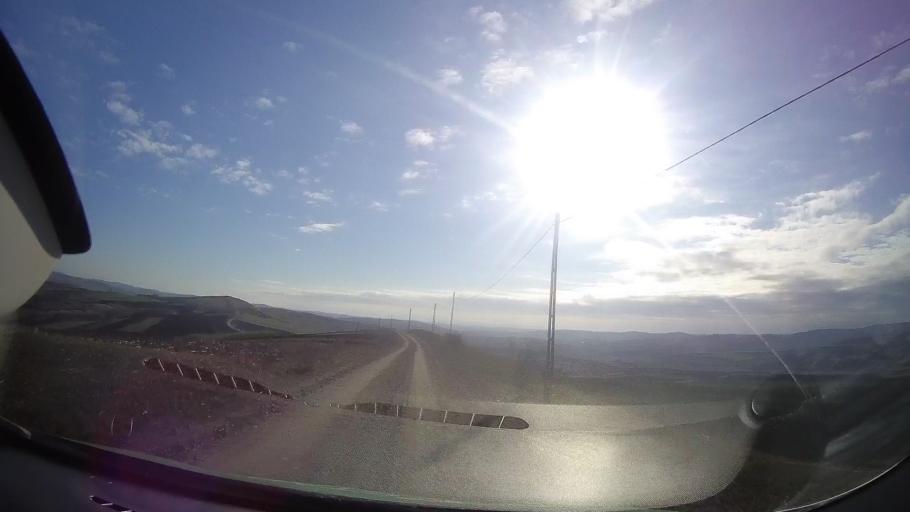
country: RO
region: Mures
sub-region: Comuna Papiu Ilarian
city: Papiu Ilarian
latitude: 46.5886
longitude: 24.2223
